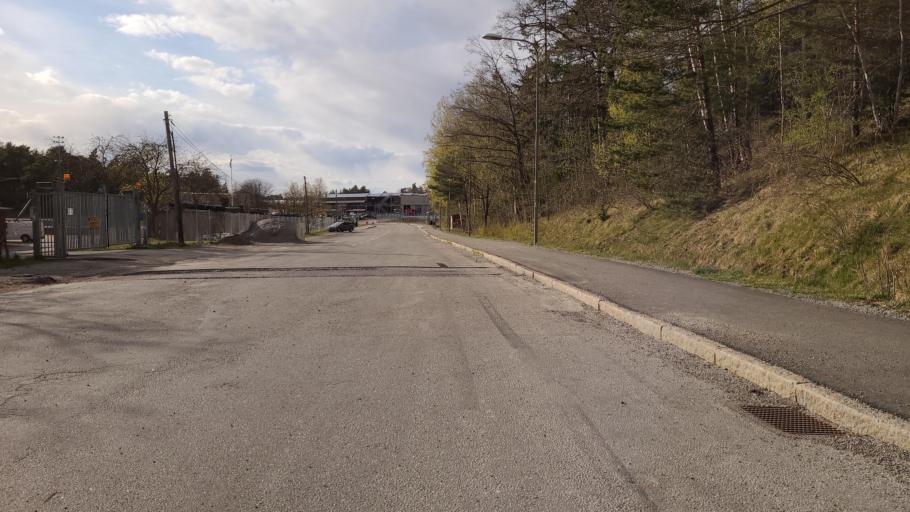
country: SE
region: Stockholm
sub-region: Stockholms Kommun
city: Arsta
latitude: 59.2624
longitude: 18.0712
